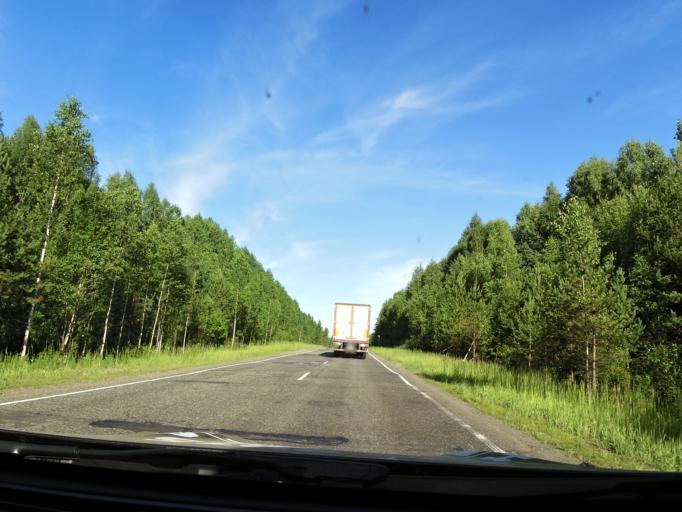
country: RU
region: Kirov
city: Chernaya Kholunitsa
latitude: 58.8767
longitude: 51.4740
